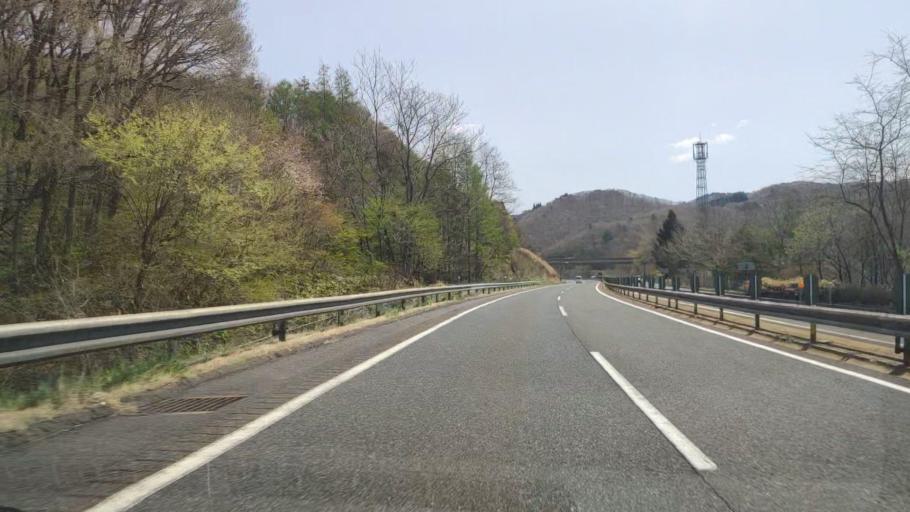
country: JP
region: Iwate
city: Ichinohe
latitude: 40.2197
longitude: 141.2404
